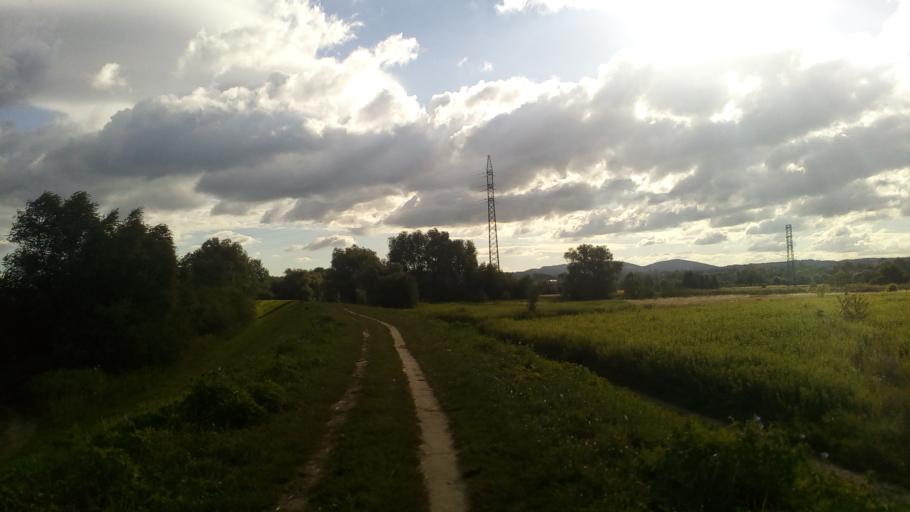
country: PL
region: Lesser Poland Voivodeship
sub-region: Powiat nowosadecki
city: Chelmiec
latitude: 49.5983
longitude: 20.6658
